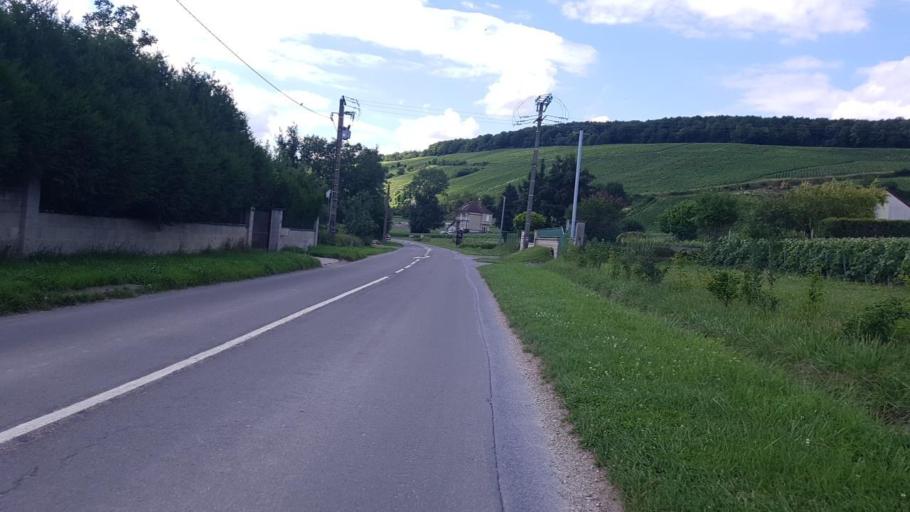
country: FR
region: Picardie
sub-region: Departement de l'Aisne
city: Crezancy
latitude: 49.0822
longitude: 3.5590
